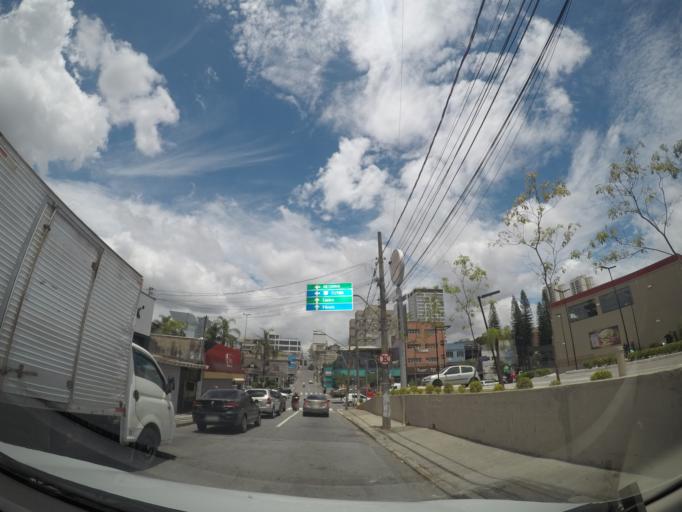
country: BR
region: Sao Paulo
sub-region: Guarulhos
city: Guarulhos
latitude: -23.4667
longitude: -46.5235
